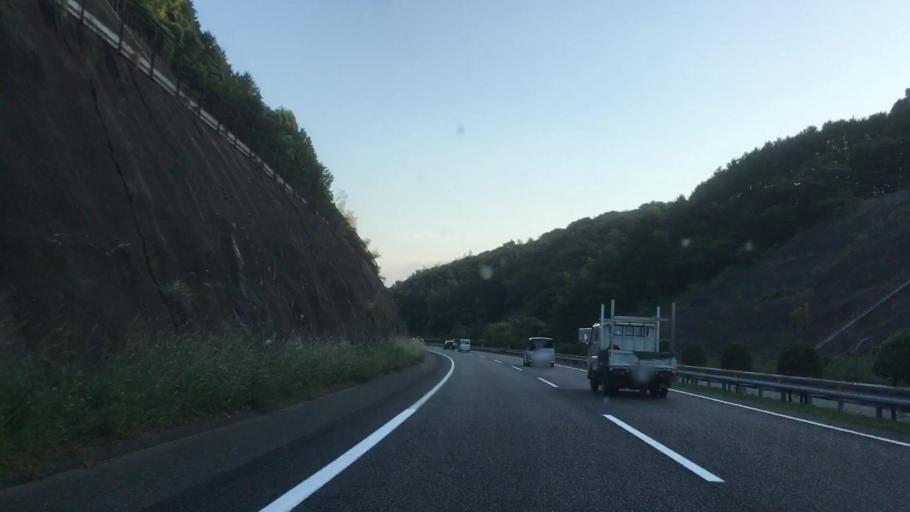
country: JP
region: Yamaguchi
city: Shimonoseki
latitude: 33.9035
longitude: 130.9715
